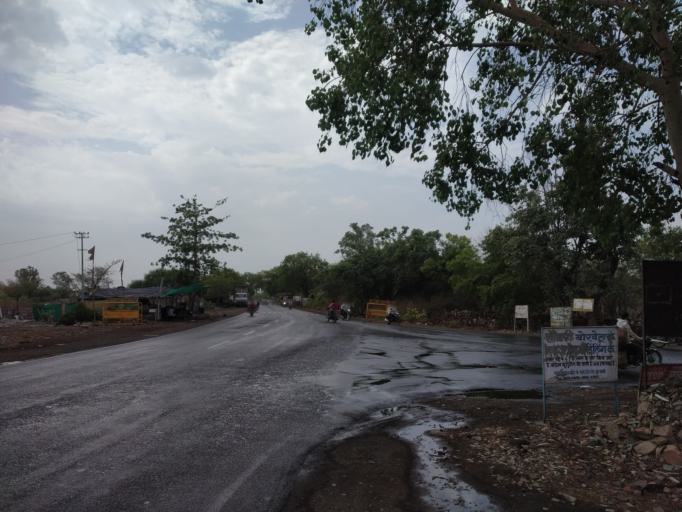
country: IN
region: Rajasthan
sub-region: Jhalawar
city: Jhalrapatan
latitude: 24.5342
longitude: 76.1896
